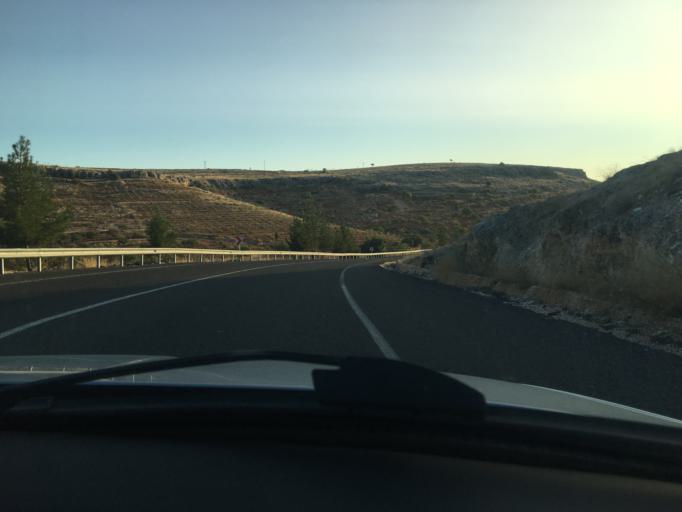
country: TR
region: Sanliurfa
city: Halfeti
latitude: 37.2244
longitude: 37.9597
